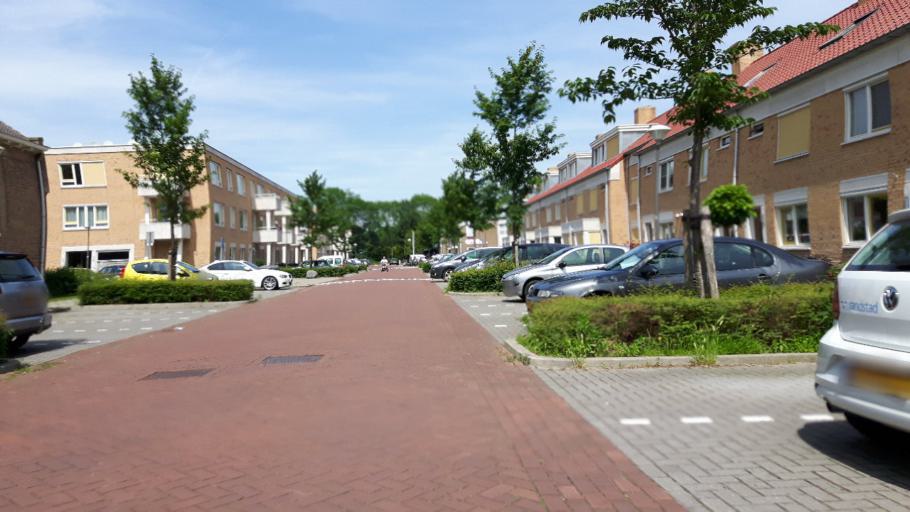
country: NL
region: Utrecht
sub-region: Gemeente Woerden
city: Woerden
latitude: 52.0903
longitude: 4.8790
